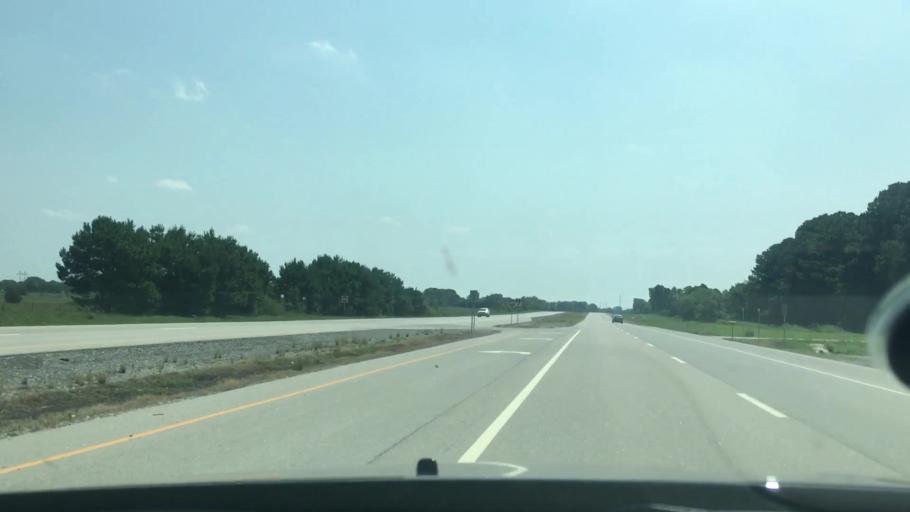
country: US
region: Oklahoma
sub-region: Atoka County
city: Atoka
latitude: 34.3408
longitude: -96.0671
